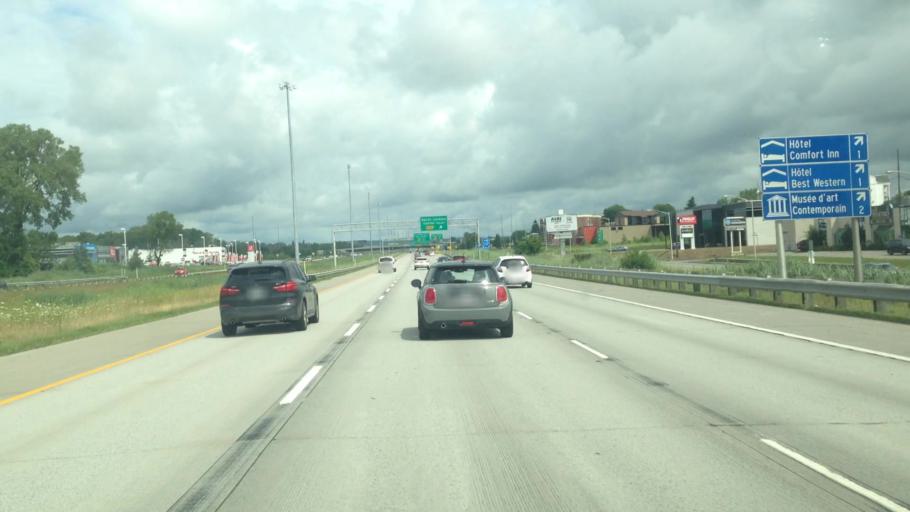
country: CA
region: Quebec
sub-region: Laurentides
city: Saint-Jerome
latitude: 45.7706
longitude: -74.0203
